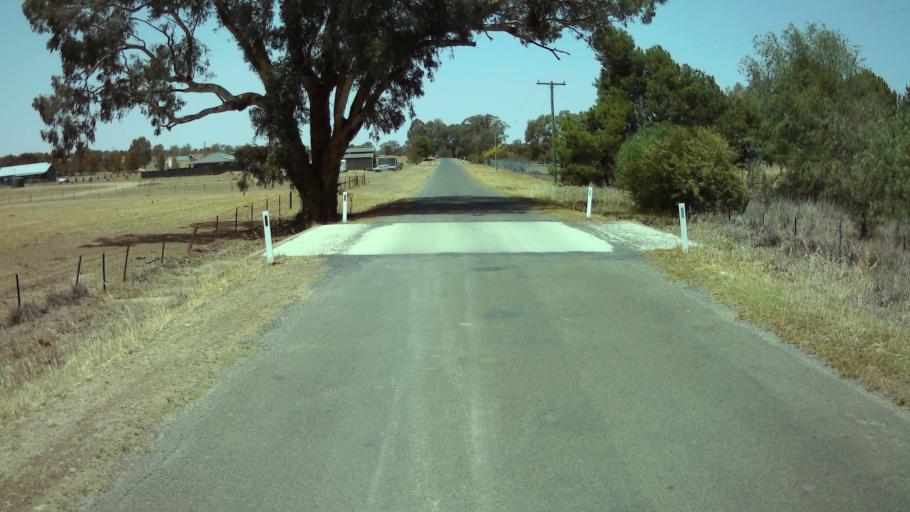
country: AU
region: New South Wales
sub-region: Weddin
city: Grenfell
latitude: -33.9039
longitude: 148.1516
